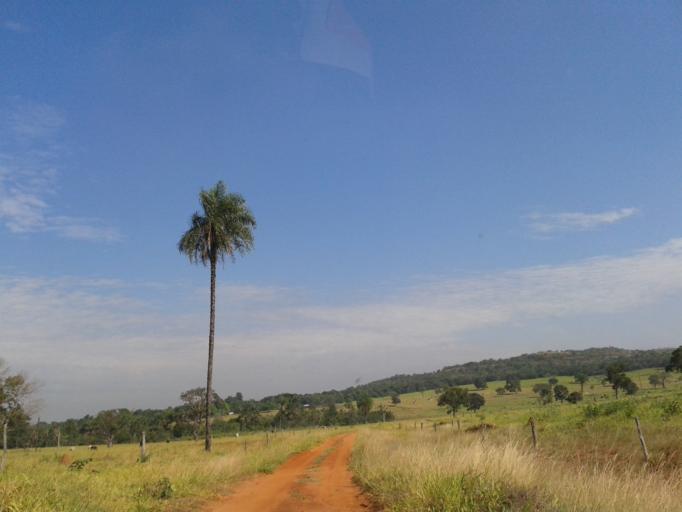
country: BR
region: Minas Gerais
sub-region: Campina Verde
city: Campina Verde
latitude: -19.3910
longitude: -49.6283
